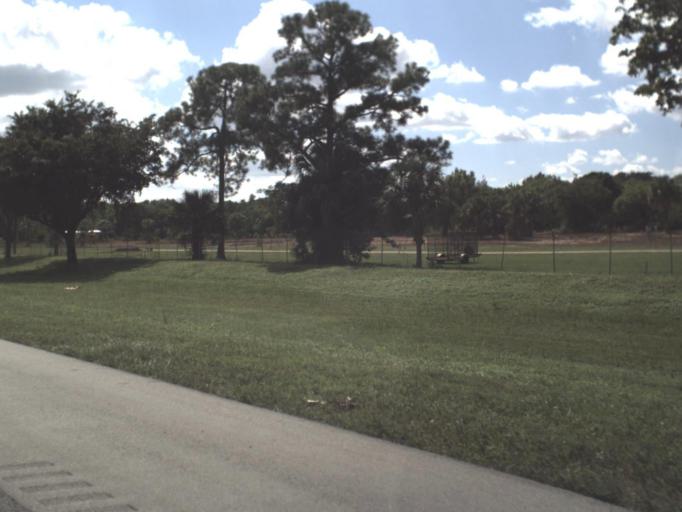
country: US
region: Florida
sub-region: Broward County
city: Coconut Creek
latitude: 26.2852
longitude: -80.1692
